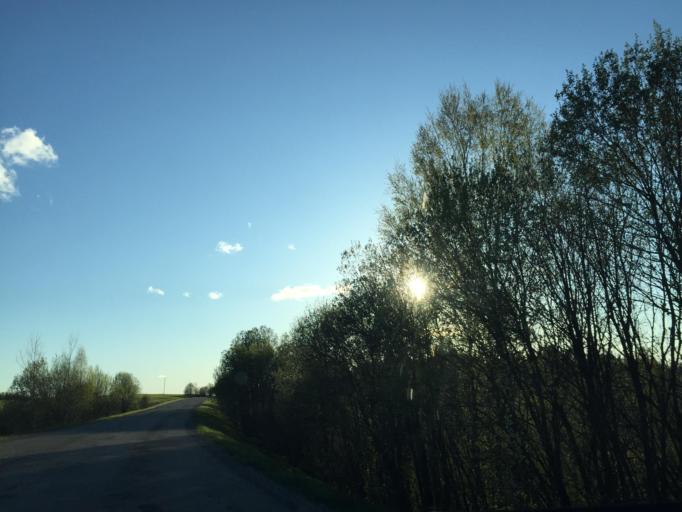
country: LV
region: Ergli
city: Ergli
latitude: 56.8673
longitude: 25.7698
